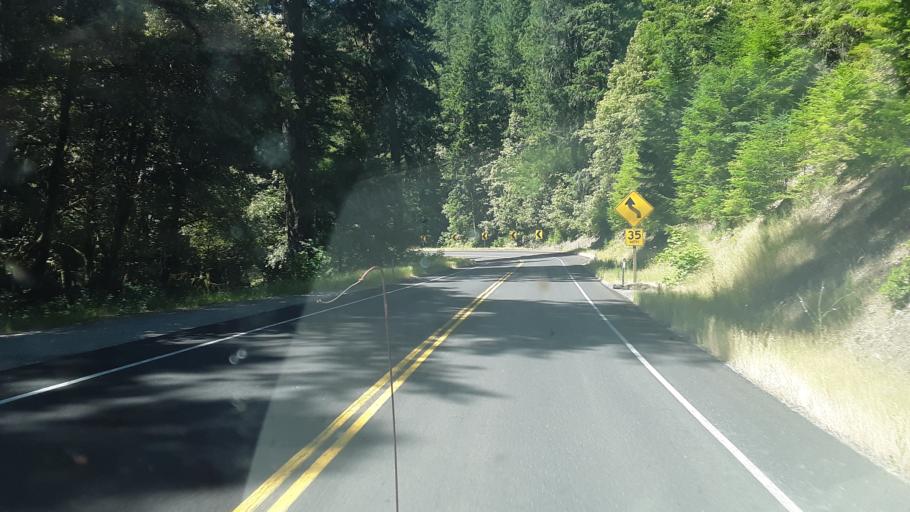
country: US
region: Oregon
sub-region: Josephine County
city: Cave Junction
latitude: 41.9349
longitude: -123.7560
